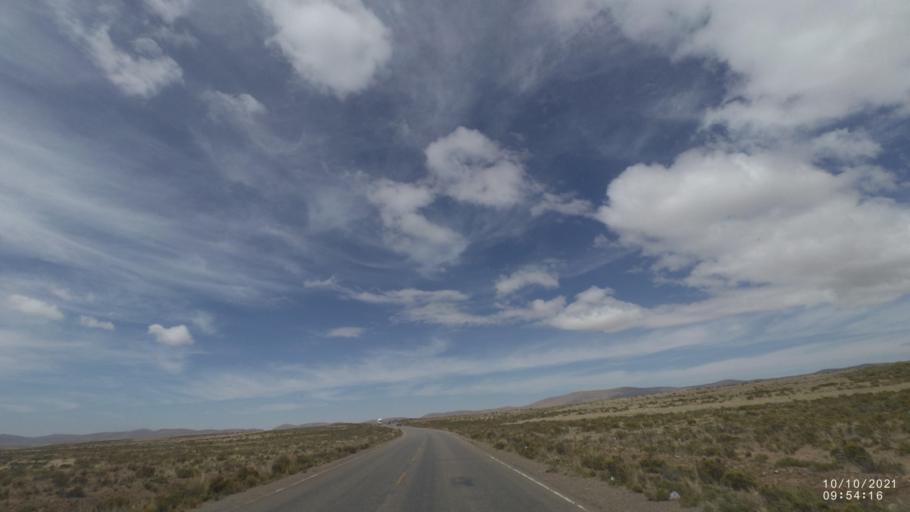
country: BO
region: La Paz
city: Colquiri
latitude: -17.2906
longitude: -67.3568
